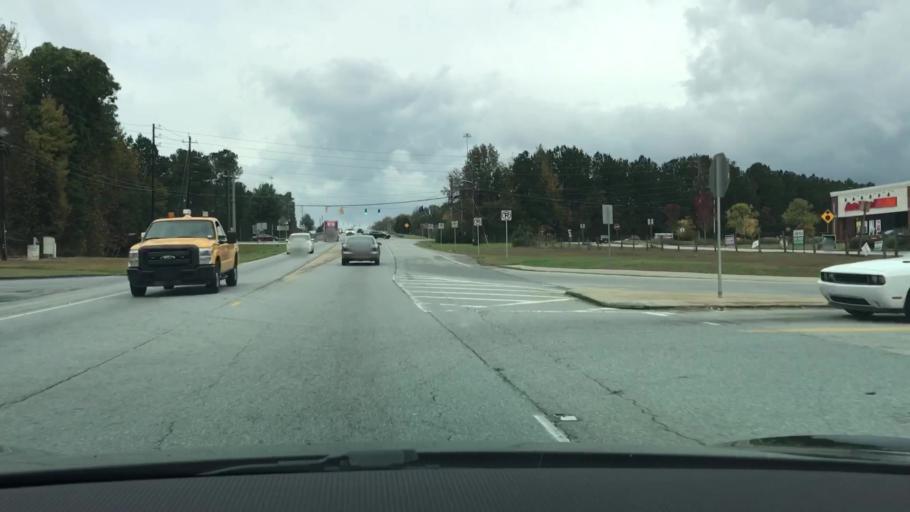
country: US
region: Georgia
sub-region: Greene County
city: Greensboro
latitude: 33.5481
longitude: -83.2034
